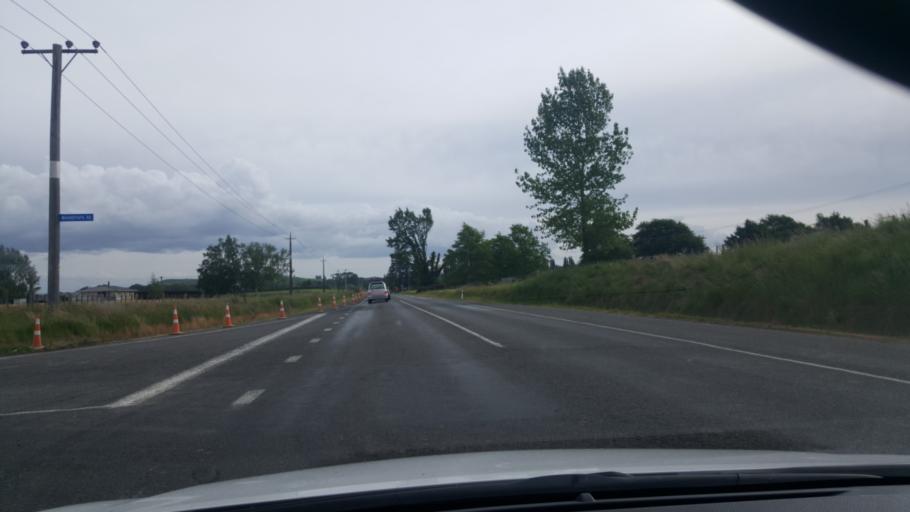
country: NZ
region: Bay of Plenty
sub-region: Rotorua District
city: Rotorua
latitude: -38.4044
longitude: 176.3280
